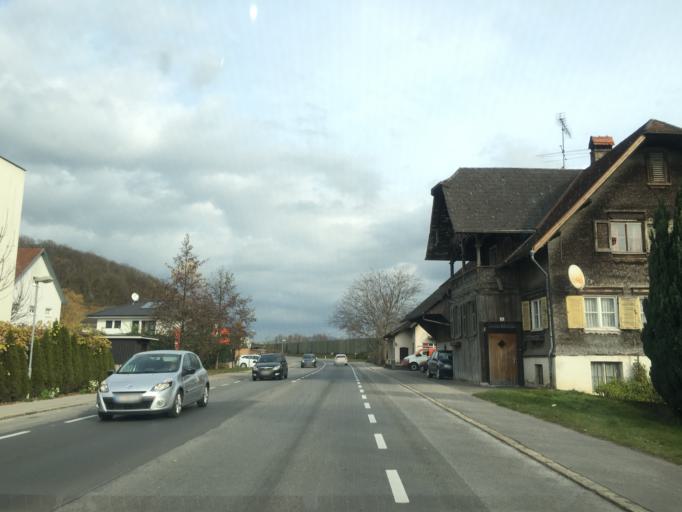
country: AT
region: Vorarlberg
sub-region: Politischer Bezirk Feldkirch
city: Gotzis
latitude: 47.3188
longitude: 9.6226
